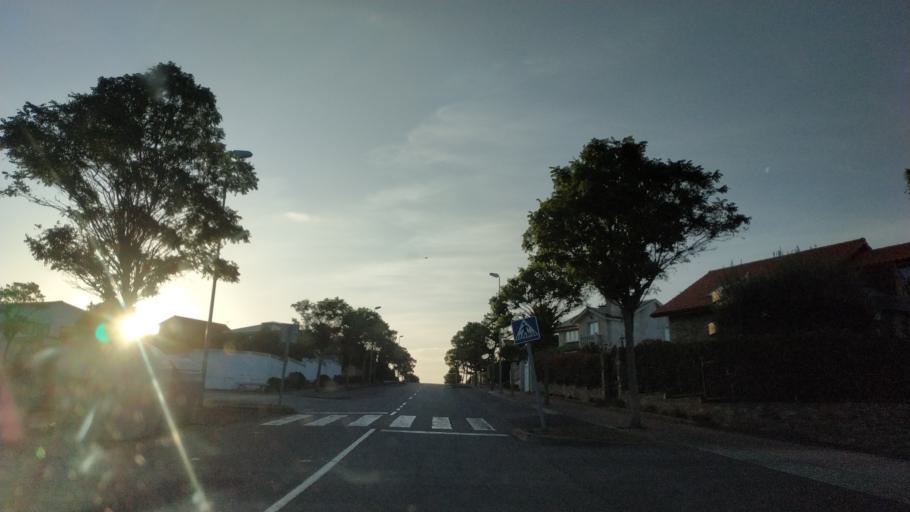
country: ES
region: Galicia
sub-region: Provincia da Coruna
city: Oleiros
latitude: 43.3705
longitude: -8.3400
